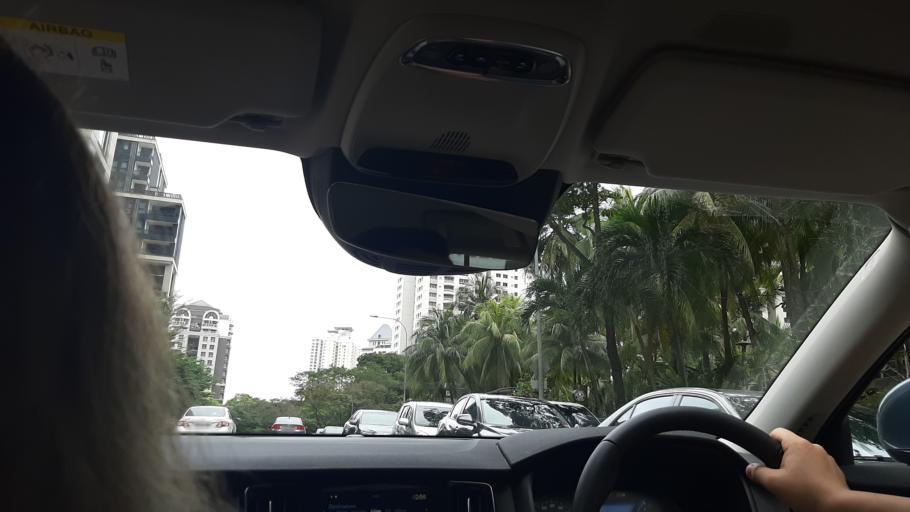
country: MY
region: Kuala Lumpur
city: Kuala Lumpur
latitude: 3.1668
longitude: 101.6528
